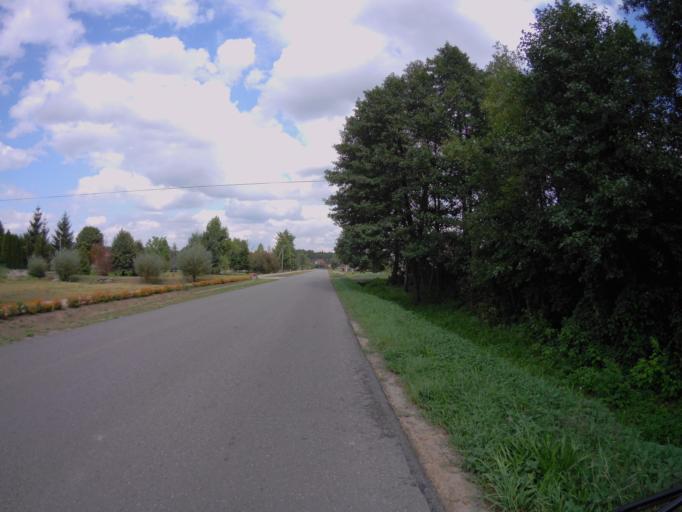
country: PL
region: Subcarpathian Voivodeship
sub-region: Powiat lezajski
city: Brzoza Krolewska
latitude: 50.2695
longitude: 22.3490
